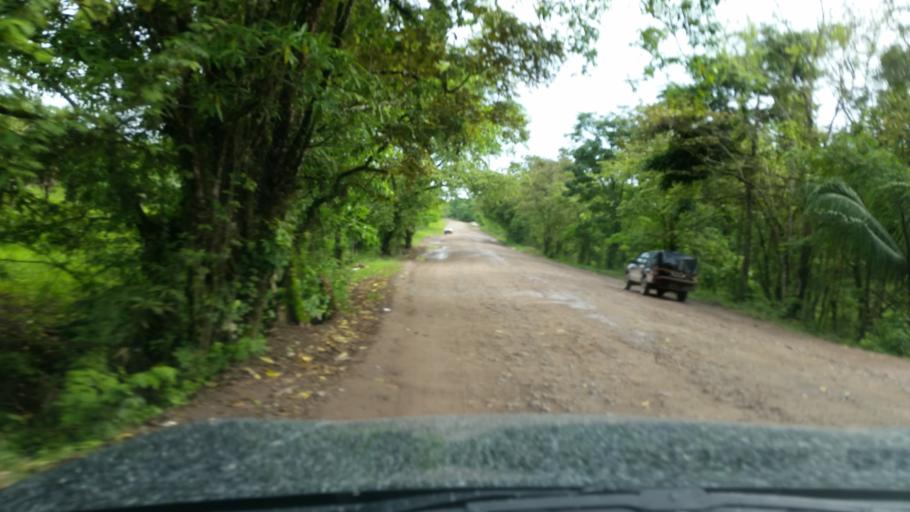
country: NI
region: Atlantico Norte (RAAN)
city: Siuna
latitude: 13.4698
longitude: -84.8455
